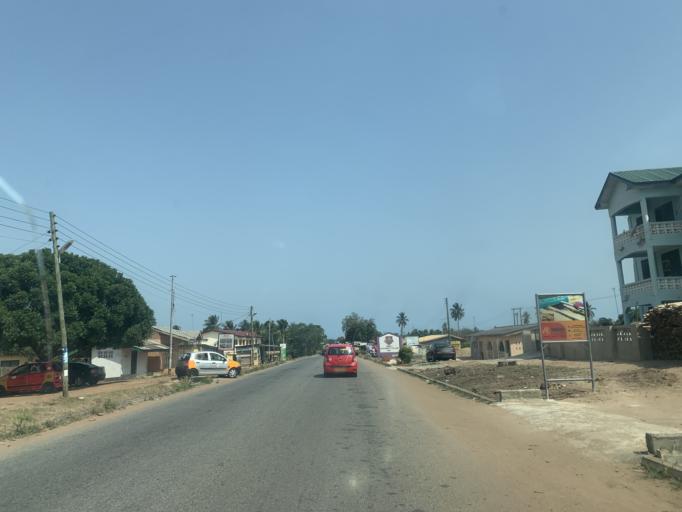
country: GH
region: Central
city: Winneba
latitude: 5.3965
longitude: -0.6489
